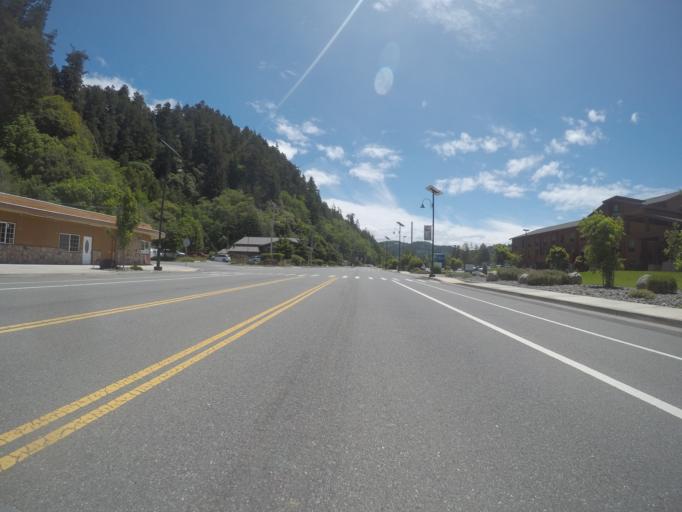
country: US
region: California
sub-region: Del Norte County
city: Bertsch-Oceanview
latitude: 41.5302
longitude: -124.0391
